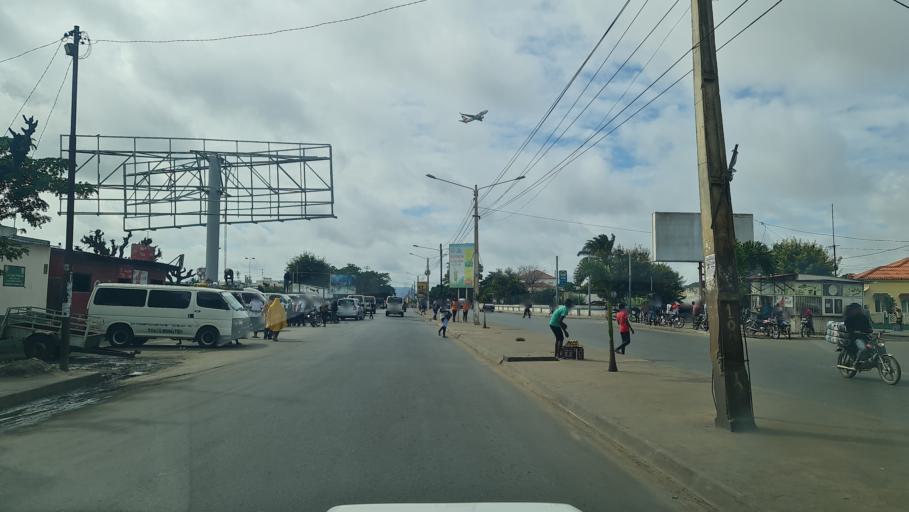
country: MZ
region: Nampula
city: Nampula
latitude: -15.1139
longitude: 39.2653
